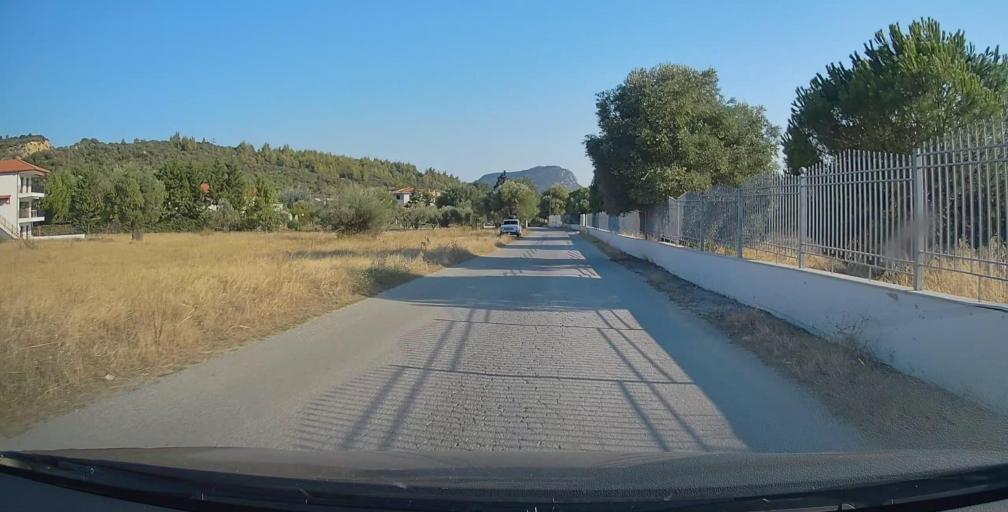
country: GR
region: Central Macedonia
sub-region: Nomos Chalkidikis
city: Sykia
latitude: 39.9974
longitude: 23.8890
